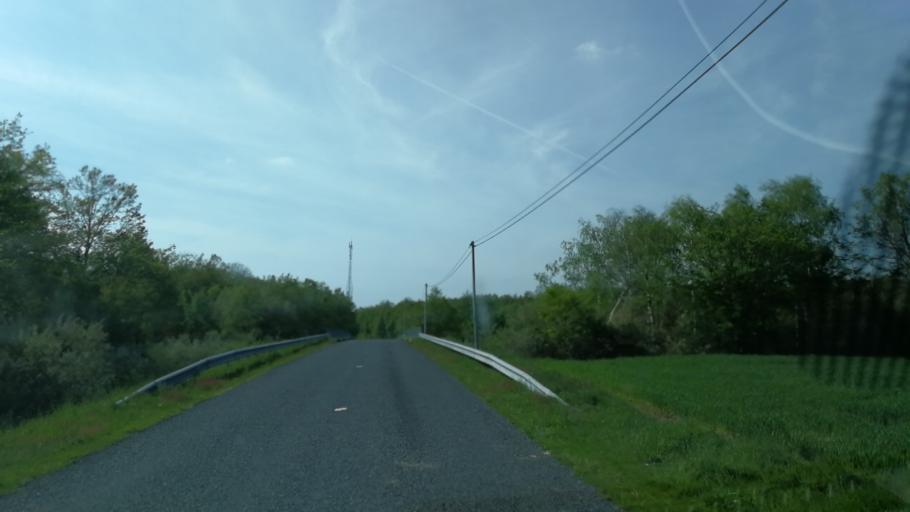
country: FR
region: Auvergne
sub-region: Departement de l'Allier
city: Neuilly-le-Real
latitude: 46.5122
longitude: 3.4589
